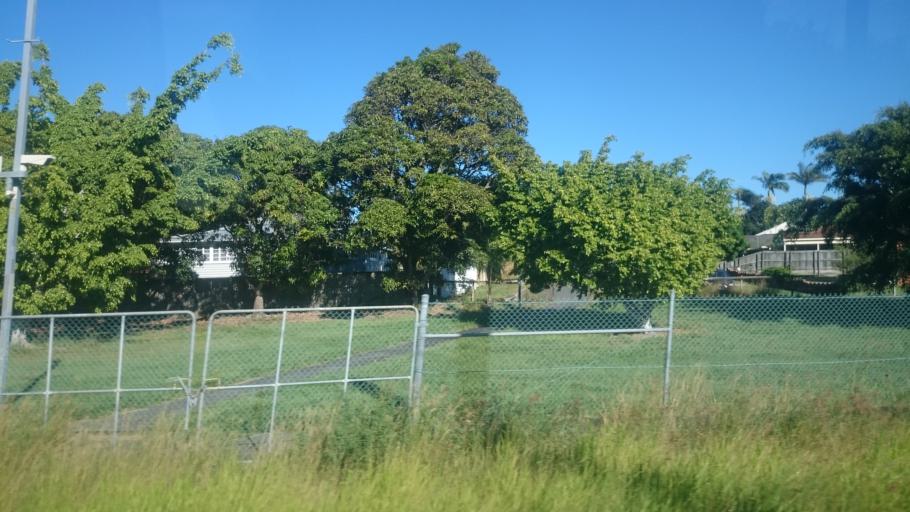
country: AU
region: Queensland
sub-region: Brisbane
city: Wynnum
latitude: -27.4389
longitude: 153.1654
